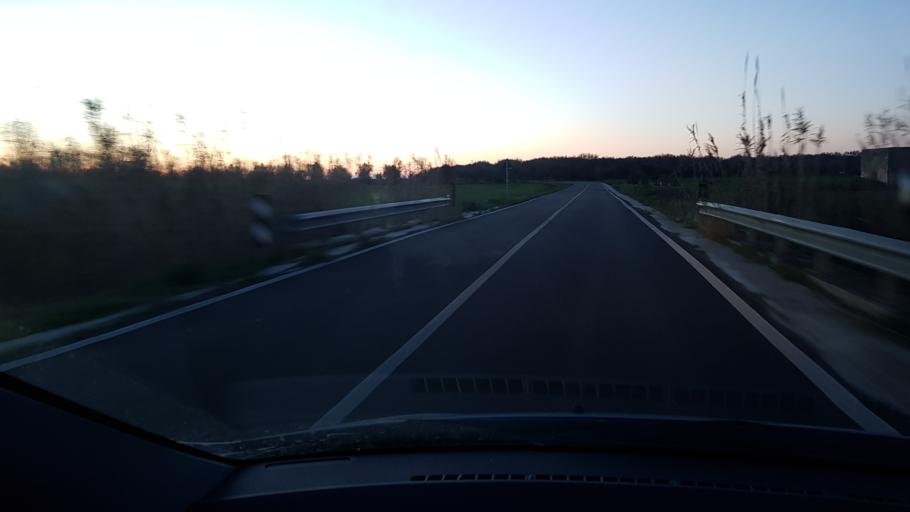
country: IT
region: Apulia
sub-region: Provincia di Brindisi
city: Tuturano
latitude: 40.5262
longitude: 17.9123
